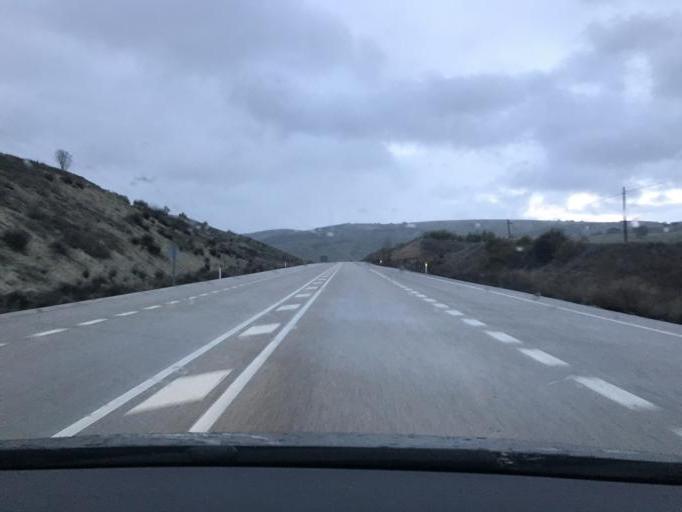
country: ES
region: Andalusia
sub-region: Provincia de Granada
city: Campotejar
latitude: 37.4538
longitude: -3.6267
